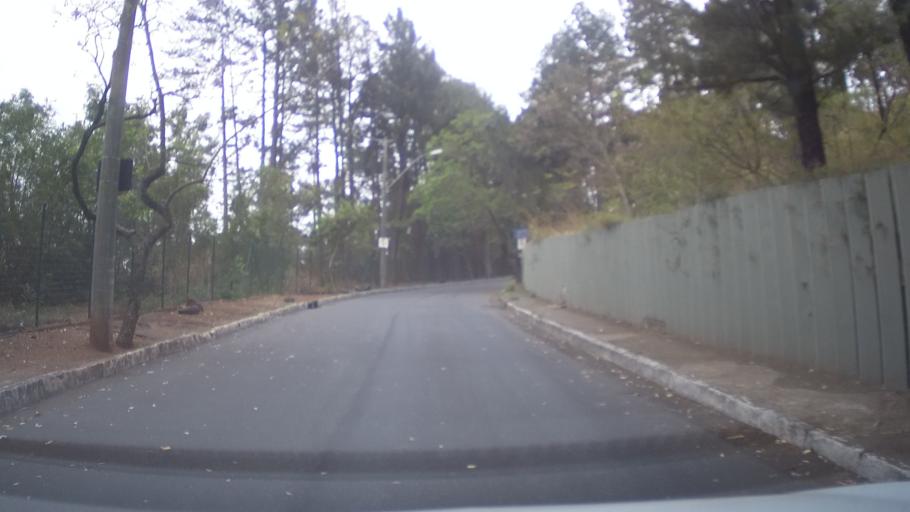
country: BR
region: Minas Gerais
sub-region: Belo Horizonte
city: Belo Horizonte
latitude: -19.9539
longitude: -43.9133
